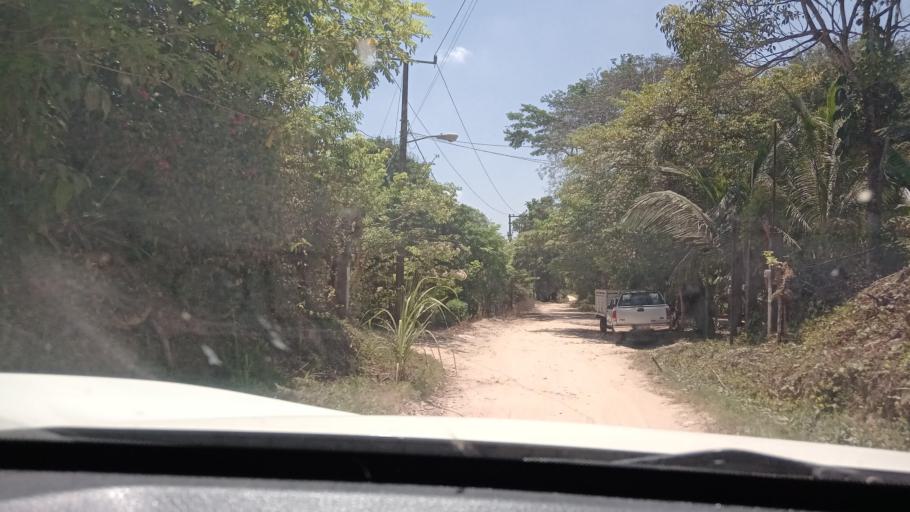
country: MX
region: Veracruz
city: Las Choapas
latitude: 17.7535
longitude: -94.1095
